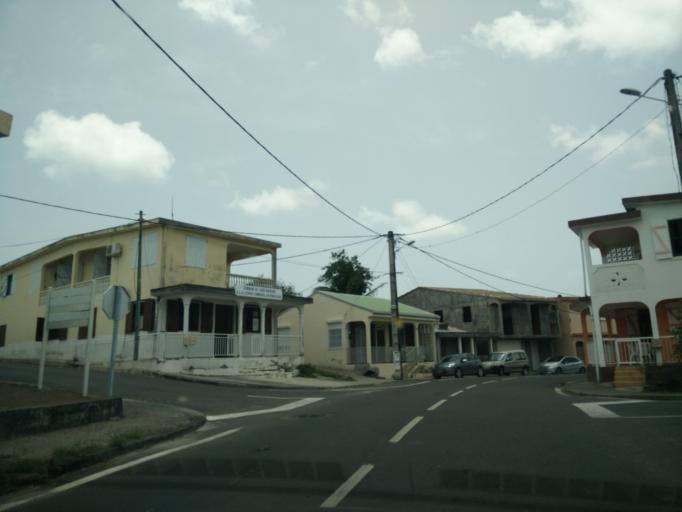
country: GP
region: Guadeloupe
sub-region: Guadeloupe
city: Anse-Bertrand
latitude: 16.4716
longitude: -61.5095
